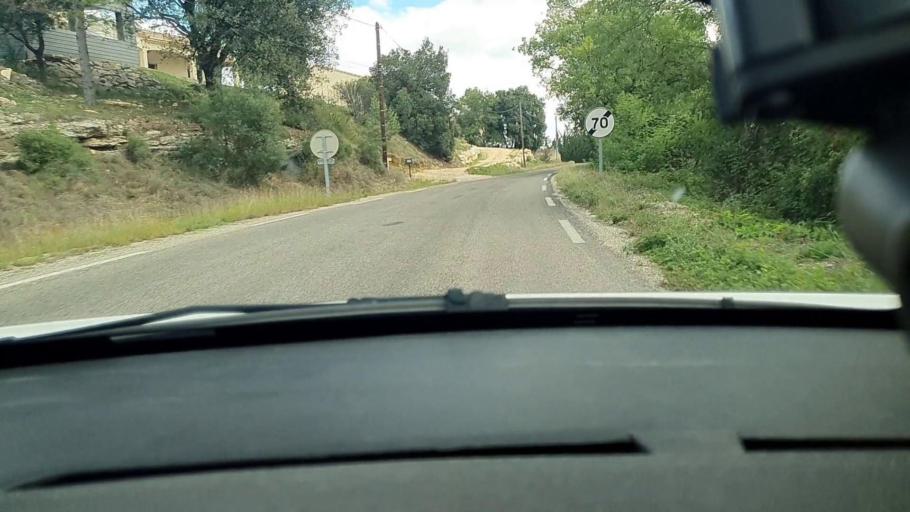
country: FR
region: Languedoc-Roussillon
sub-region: Departement du Gard
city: Les Mages
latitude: 44.2150
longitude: 4.1837
